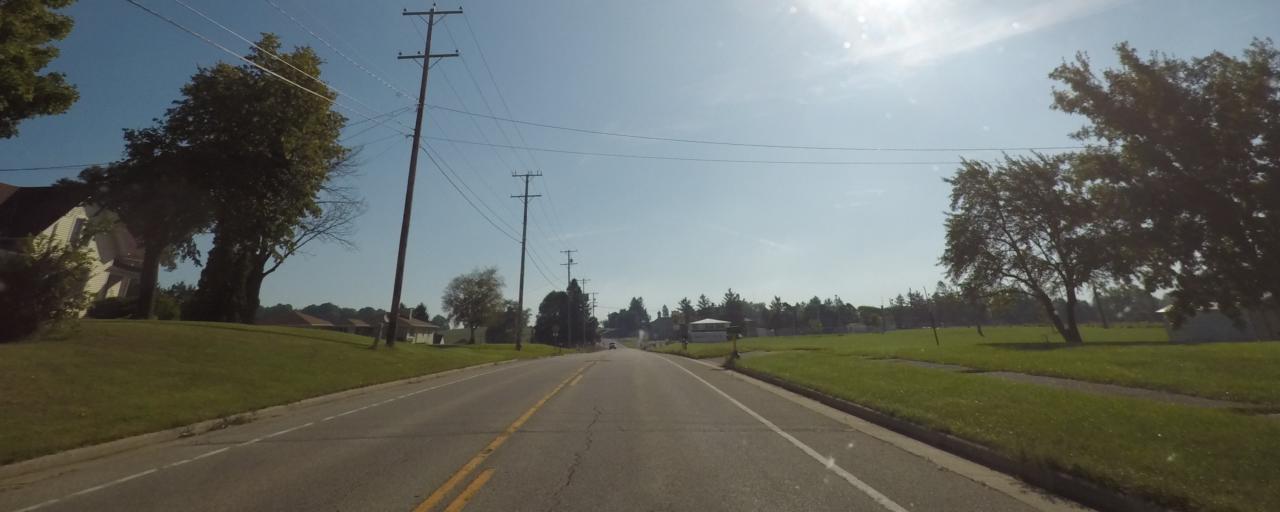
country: US
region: Wisconsin
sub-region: Jefferson County
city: Jefferson
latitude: 43.0048
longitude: -88.7859
